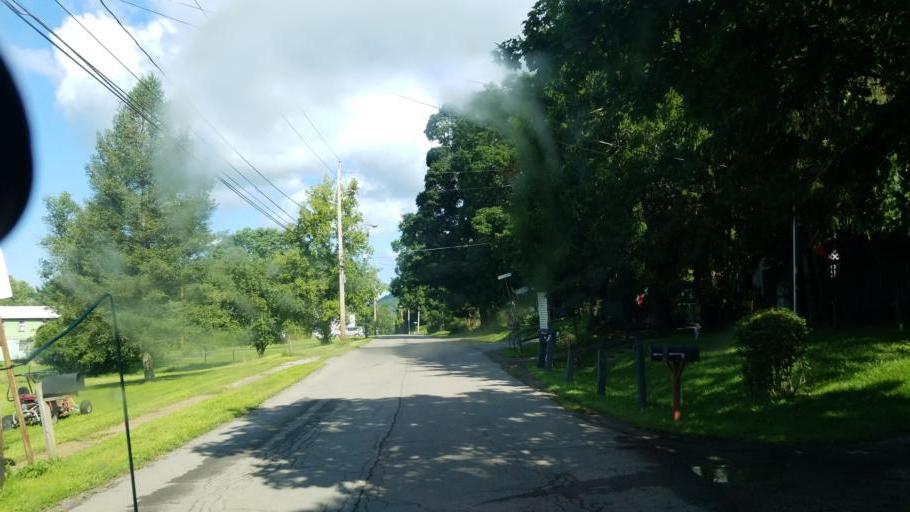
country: US
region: New York
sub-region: Steuben County
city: Canisteo
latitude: 42.2792
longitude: -77.6016
